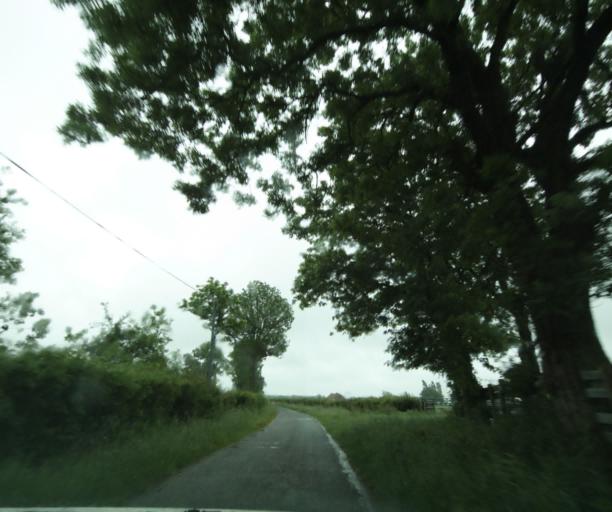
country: FR
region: Bourgogne
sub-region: Departement de Saone-et-Loire
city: Ciry-le-Noble
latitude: 46.5597
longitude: 4.3275
